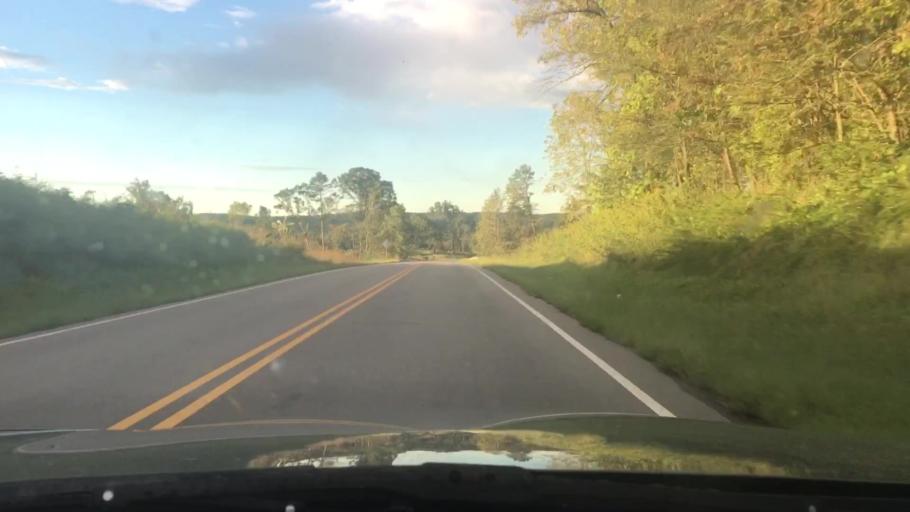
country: US
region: North Carolina
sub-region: Caswell County
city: Yanceyville
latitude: 36.3980
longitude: -79.3295
